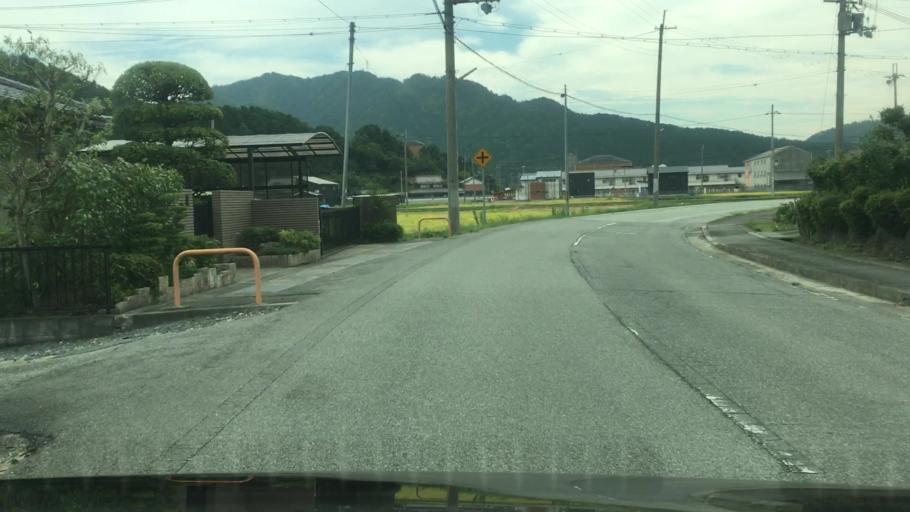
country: JP
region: Hyogo
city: Sasayama
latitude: 35.0700
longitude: 135.1843
